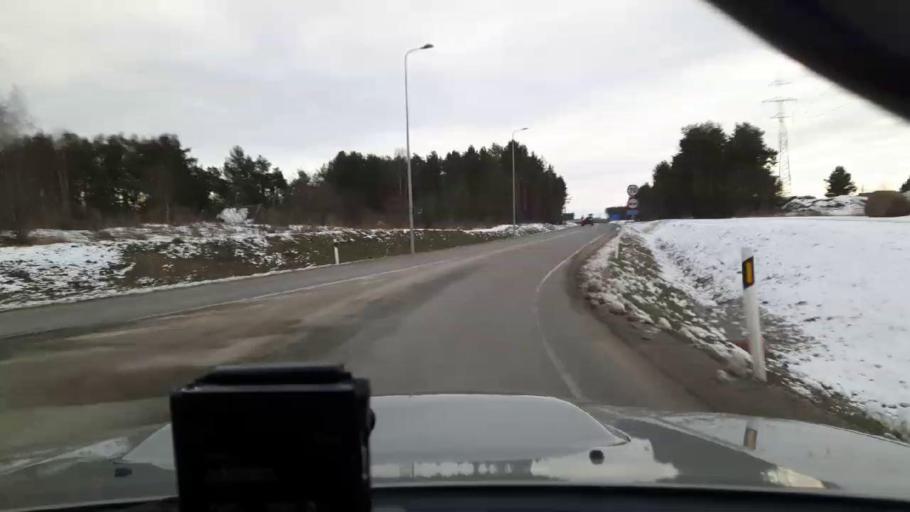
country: EE
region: Harju
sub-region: Saue vald
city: Laagri
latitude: 59.3464
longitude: 24.6002
